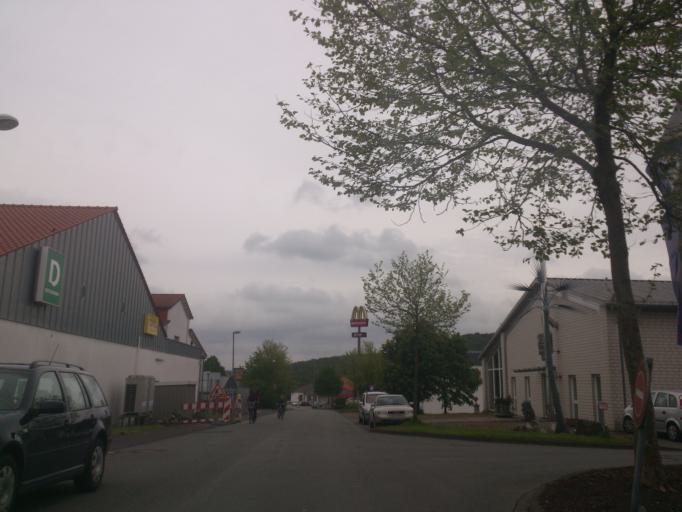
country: DE
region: North Rhine-Westphalia
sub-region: Regierungsbezirk Detmold
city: Bad Driburg
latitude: 51.7203
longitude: 9.0137
